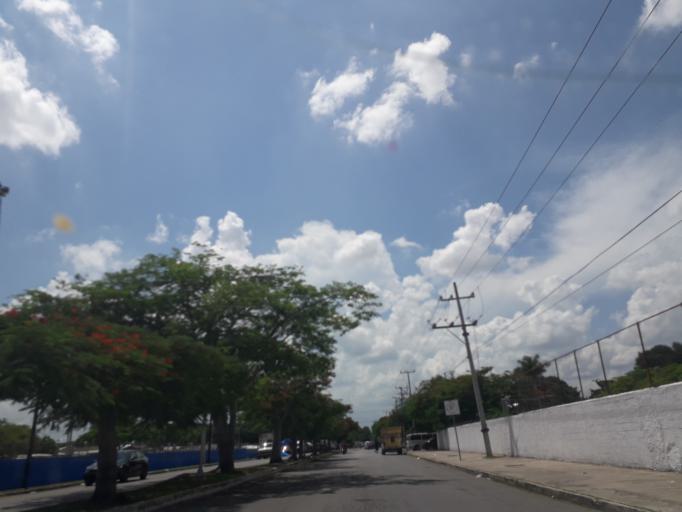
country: MX
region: Yucatan
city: Merida
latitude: 20.9692
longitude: -89.6561
